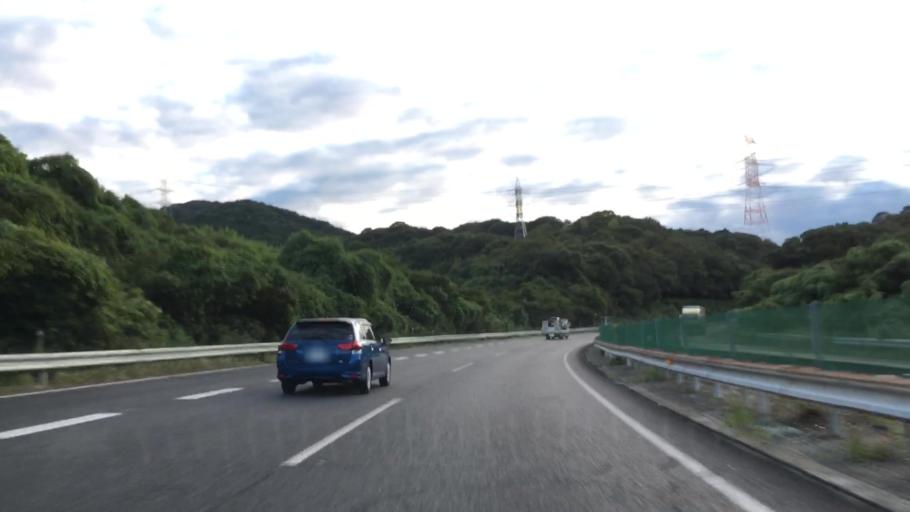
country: JP
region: Yamaguchi
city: Shimonoseki
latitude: 34.0401
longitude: 130.9826
